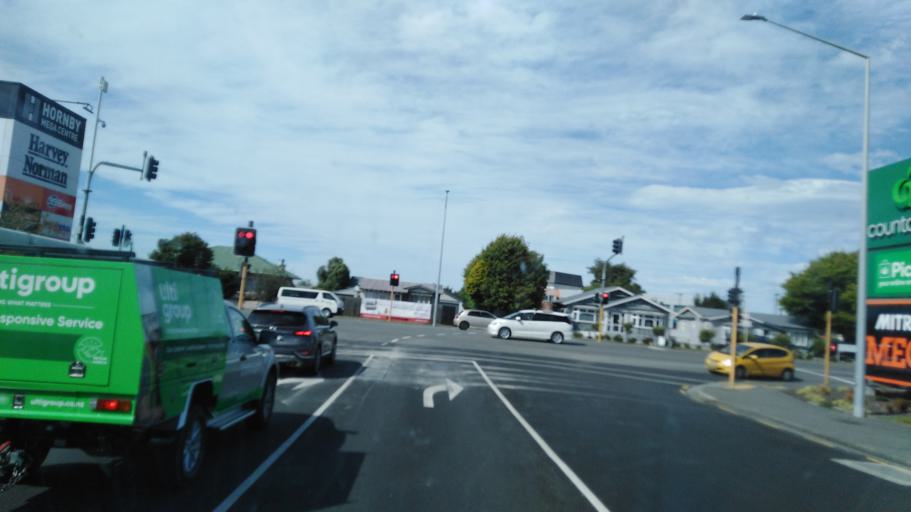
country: NZ
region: Canterbury
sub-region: Selwyn District
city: Prebbleton
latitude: -43.5427
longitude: 172.5295
